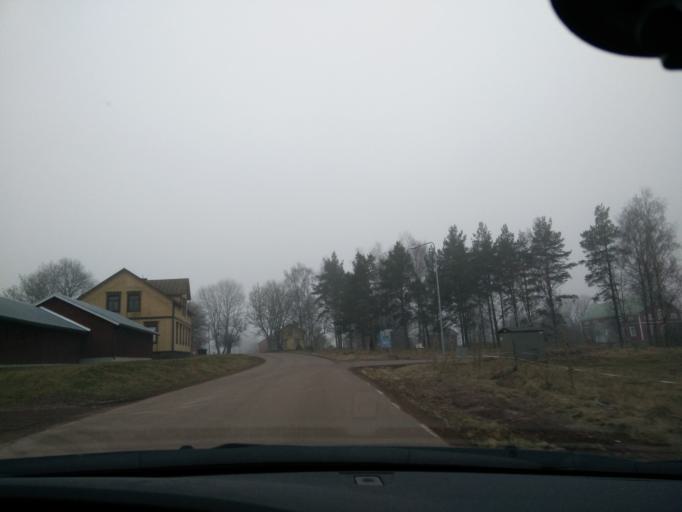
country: AX
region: Mariehamns stad
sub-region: Mariehamn
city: Mariehamn
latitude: 60.1059
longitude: 19.9001
